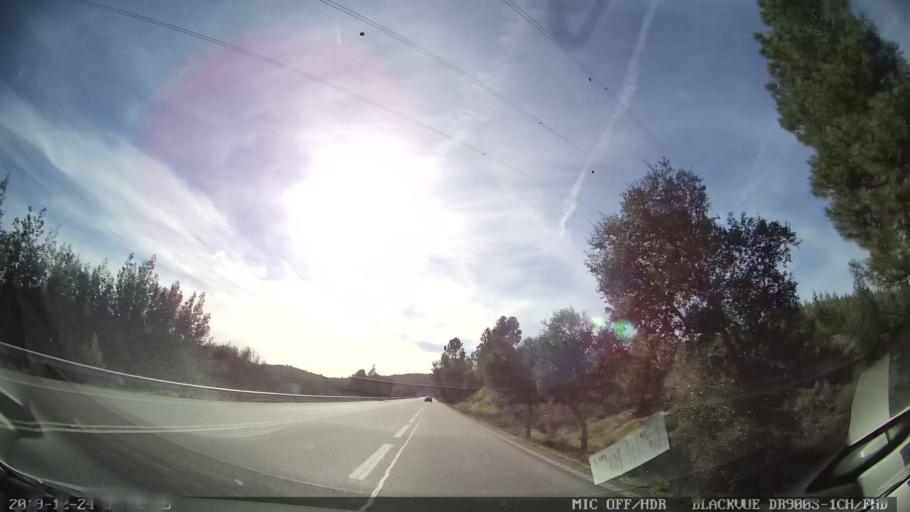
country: PT
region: Portalegre
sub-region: Nisa
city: Nisa
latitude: 39.5112
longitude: -7.7698
